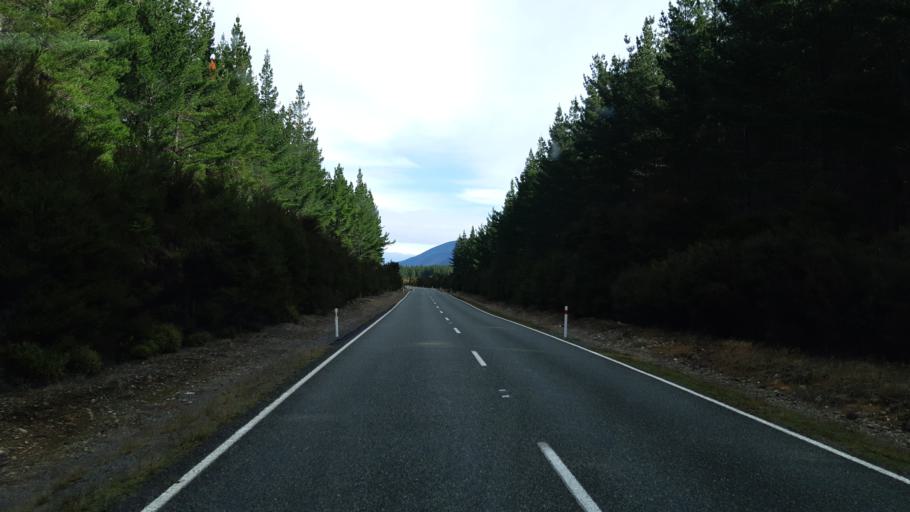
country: NZ
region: Tasman
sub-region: Tasman District
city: Wakefield
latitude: -41.7212
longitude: 173.0607
